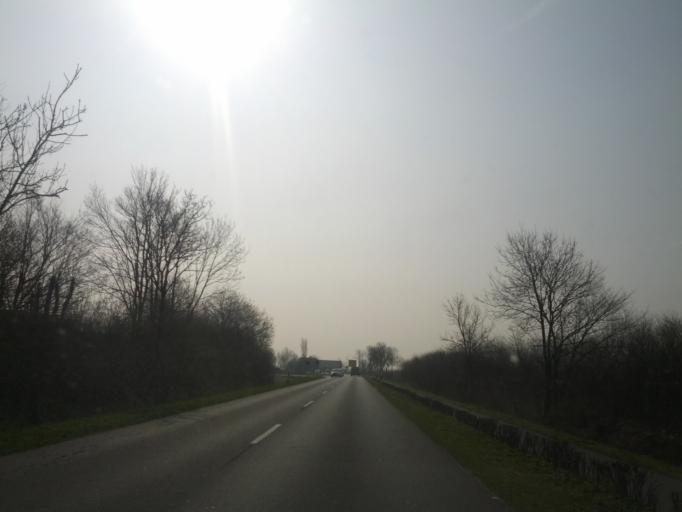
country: DE
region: Lower Saxony
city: Moorweg
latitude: 53.6731
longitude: 7.5796
